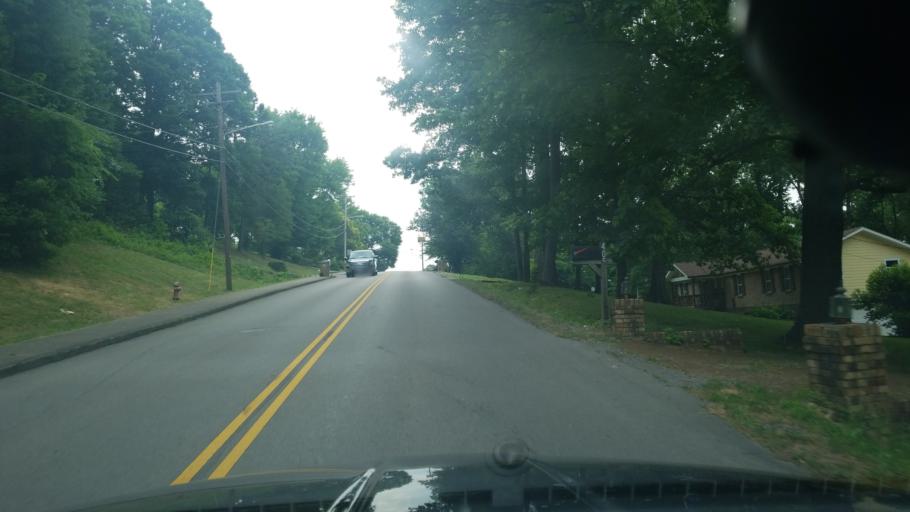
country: US
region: Tennessee
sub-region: Davidson County
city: Goodlettsville
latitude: 36.2551
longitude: -86.7431
